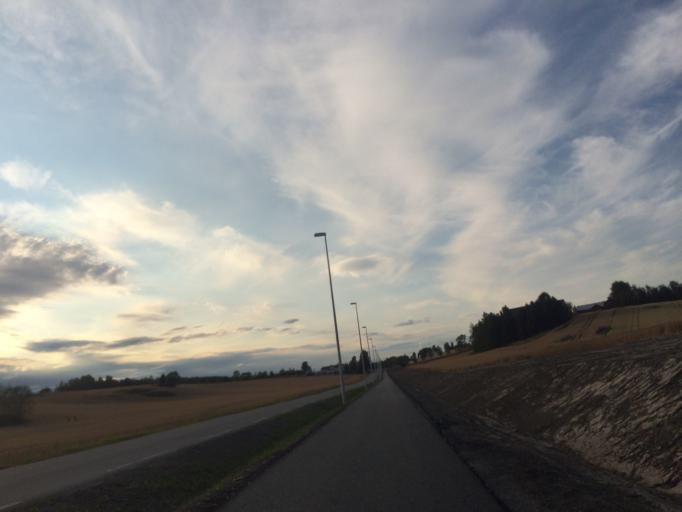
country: NO
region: Akershus
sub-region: Ski
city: Ski
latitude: 59.6860
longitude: 10.8691
